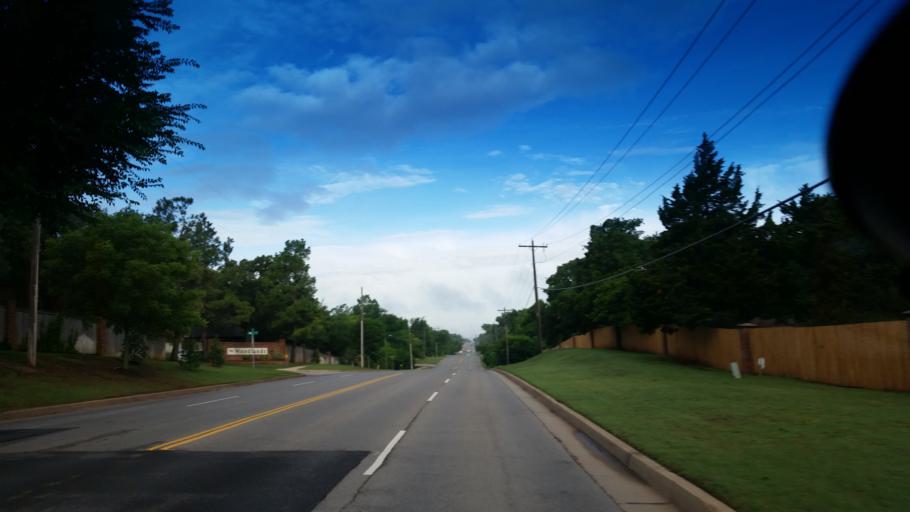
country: US
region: Oklahoma
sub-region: Oklahoma County
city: Edmond
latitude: 35.6383
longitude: -97.4447
